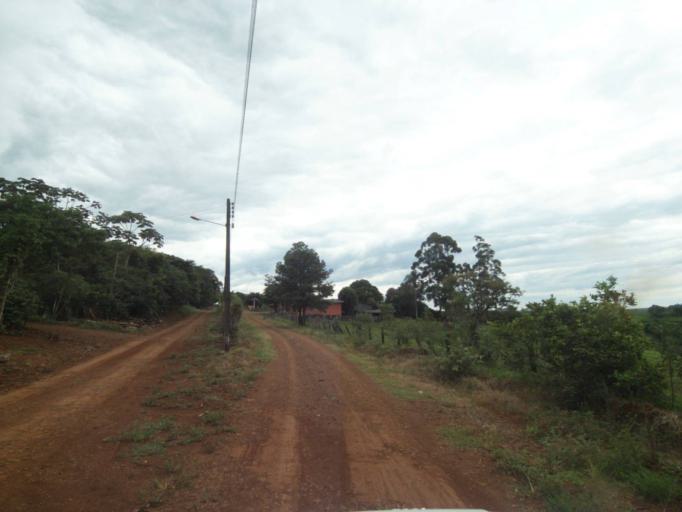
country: BR
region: Parana
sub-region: Guaraniacu
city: Guaraniacu
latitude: -24.9139
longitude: -52.9373
